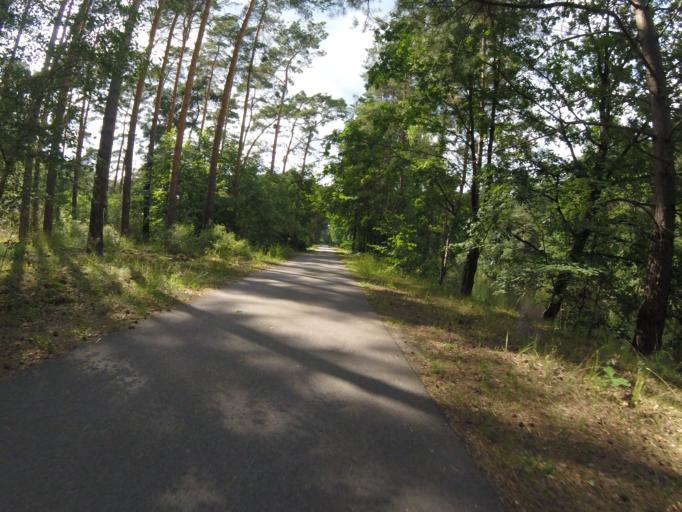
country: DE
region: Brandenburg
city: Halbe
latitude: 52.0963
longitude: 13.7826
